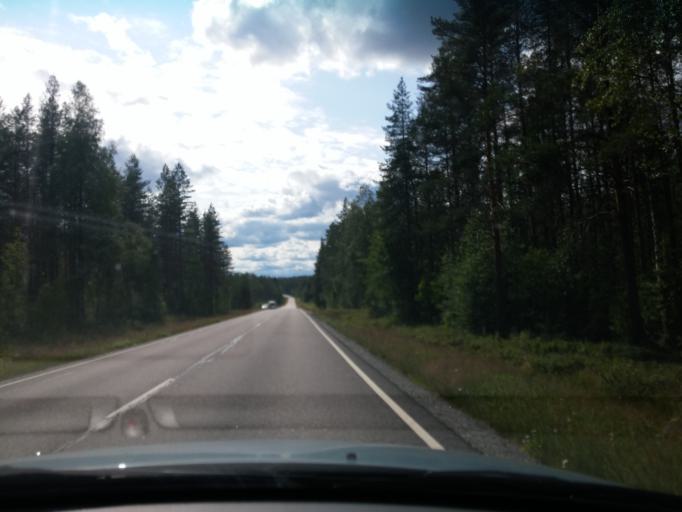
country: FI
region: Central Finland
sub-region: Saarijaervi-Viitasaari
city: Pylkoenmaeki
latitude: 62.5962
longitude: 24.6166
